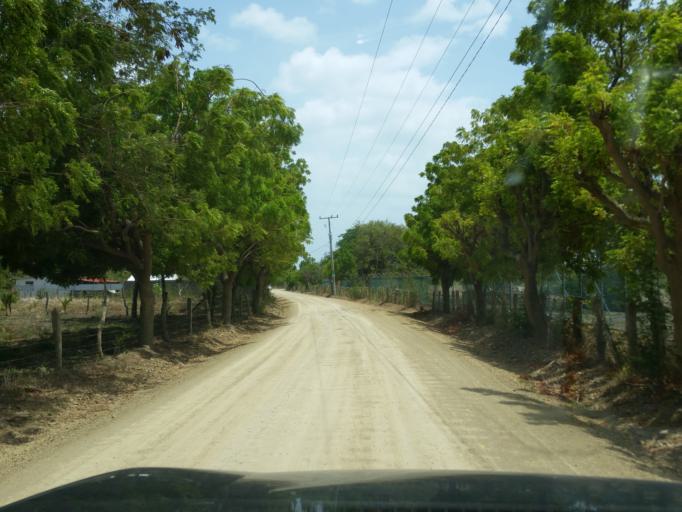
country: NI
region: Rivas
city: Tola
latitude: 11.4208
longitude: -86.0365
